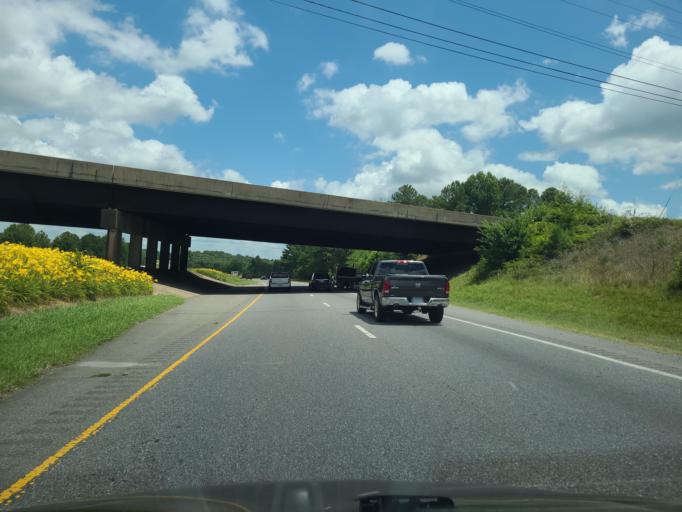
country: US
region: North Carolina
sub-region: Cleveland County
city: White Plains
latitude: 35.2467
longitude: -81.4080
